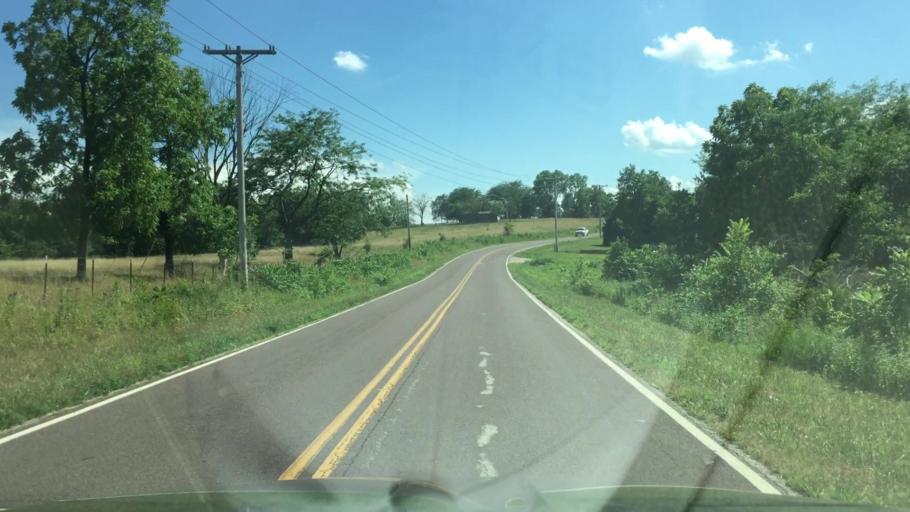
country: US
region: Missouri
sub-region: Miller County
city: Tuscumbia
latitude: 38.1286
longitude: -92.4608
